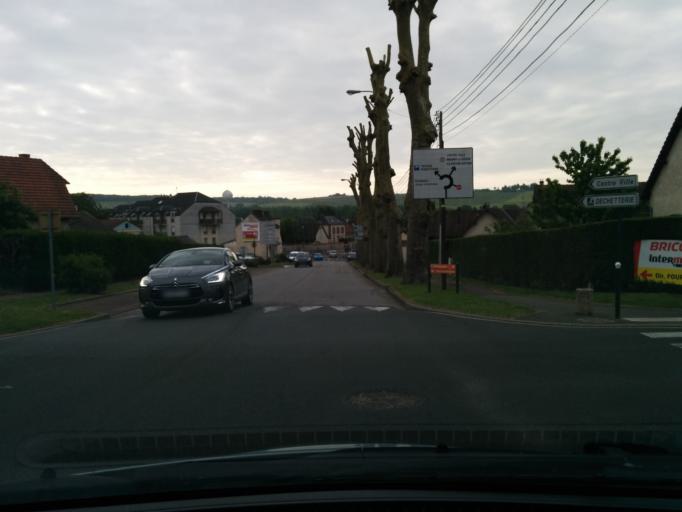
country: FR
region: Haute-Normandie
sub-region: Departement de l'Eure
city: Gasny
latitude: 49.0926
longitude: 1.6020
